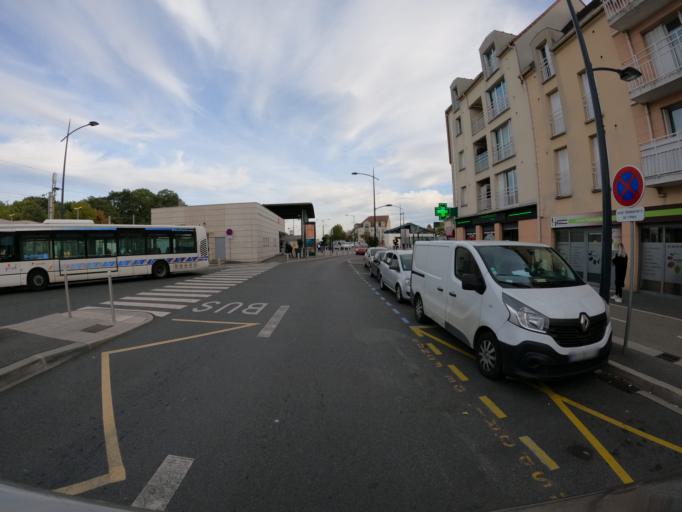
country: FR
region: Ile-de-France
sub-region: Departement de Seine-et-Marne
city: Emerainville
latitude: 48.8061
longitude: 2.6173
